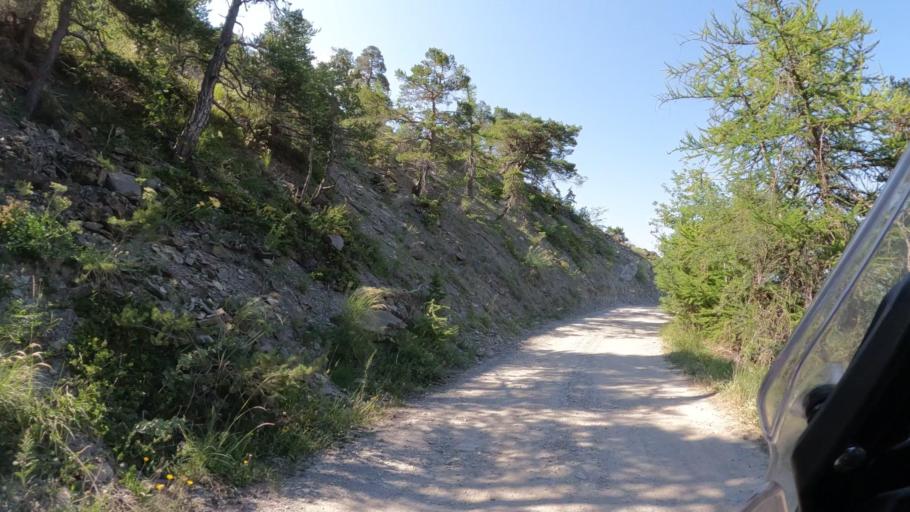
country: FR
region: Provence-Alpes-Cote d'Azur
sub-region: Departement des Hautes-Alpes
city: Embrun
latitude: 44.6004
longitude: 6.5643
